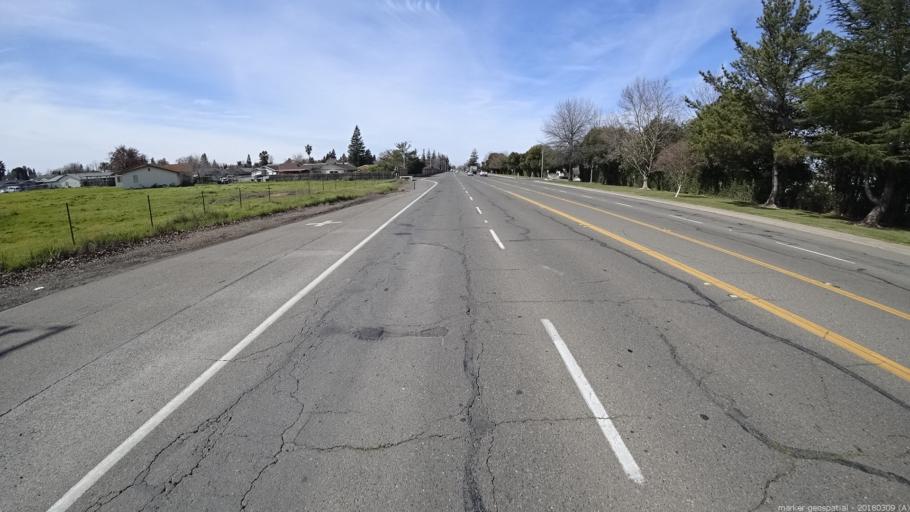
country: US
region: California
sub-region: Sacramento County
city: Florin
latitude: 38.4961
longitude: -121.3814
